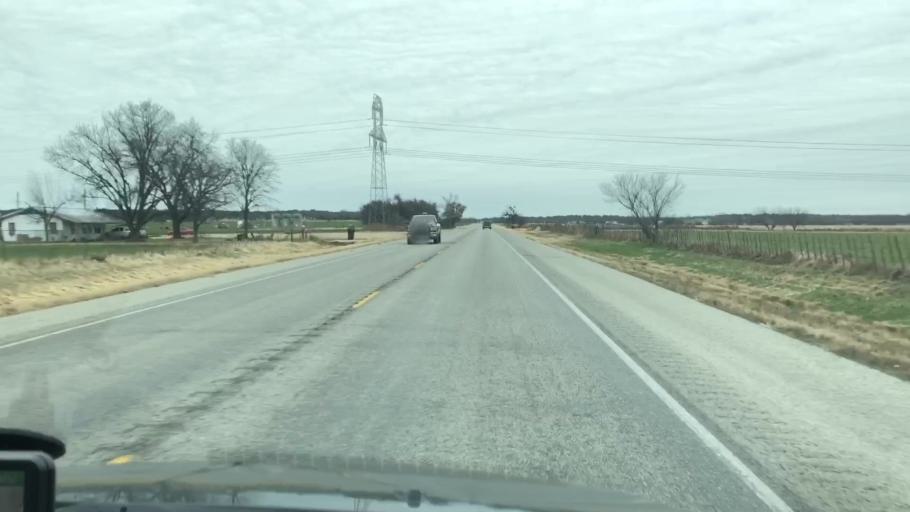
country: US
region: Texas
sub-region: Palo Pinto County
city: Mineral Wells
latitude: 32.9292
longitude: -98.0713
